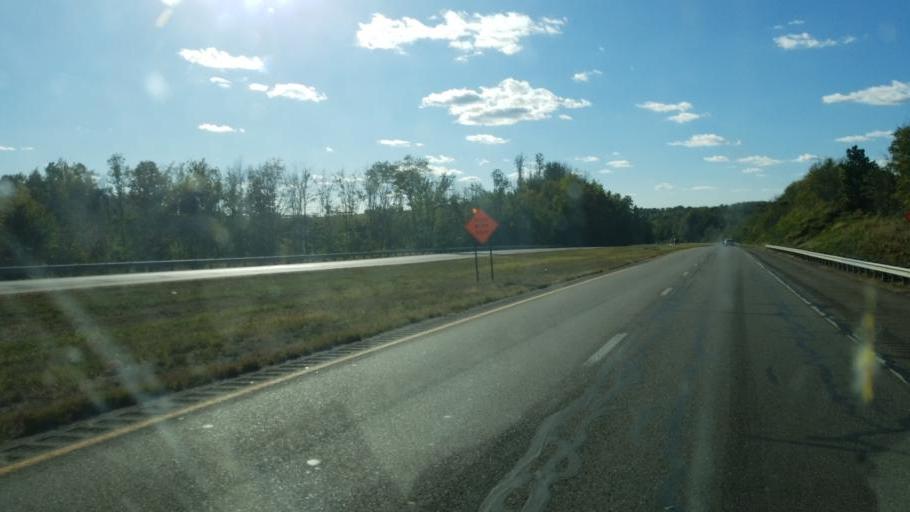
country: US
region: Ohio
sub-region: Belmont County
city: Bethesda
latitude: 40.0596
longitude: -81.0921
